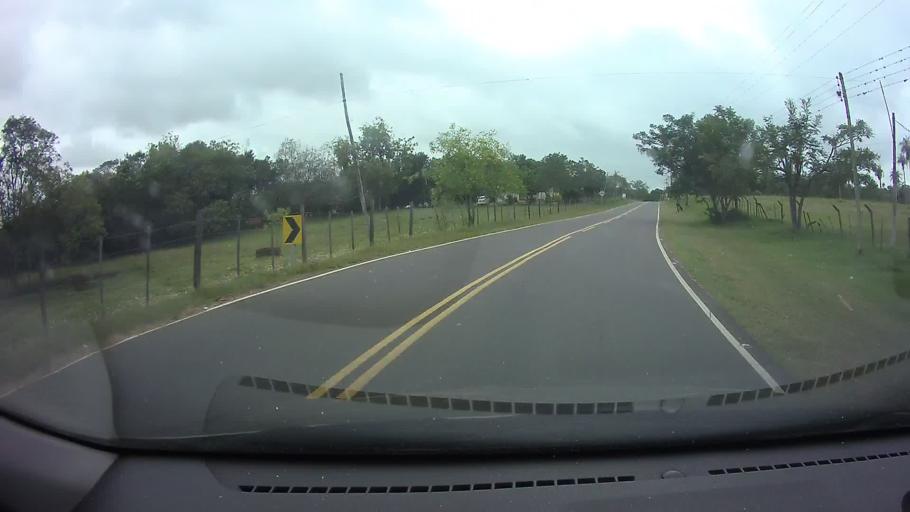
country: PY
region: Central
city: Nueva Italia
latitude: -25.6082
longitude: -57.4272
